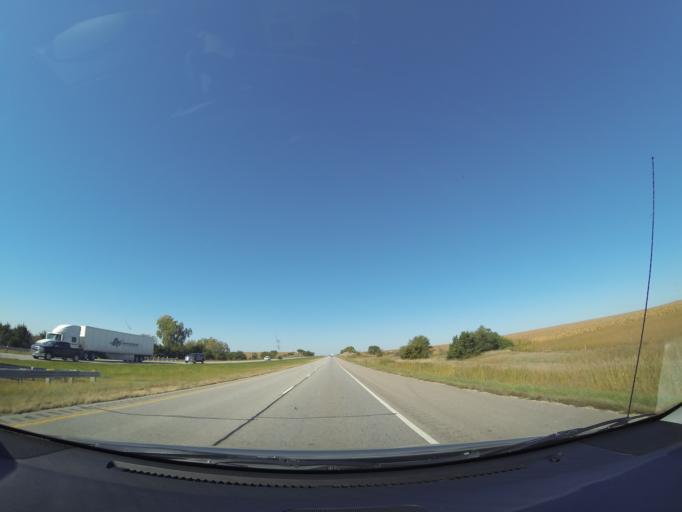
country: US
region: Nebraska
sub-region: Seward County
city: Seward
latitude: 40.8224
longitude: -97.1366
